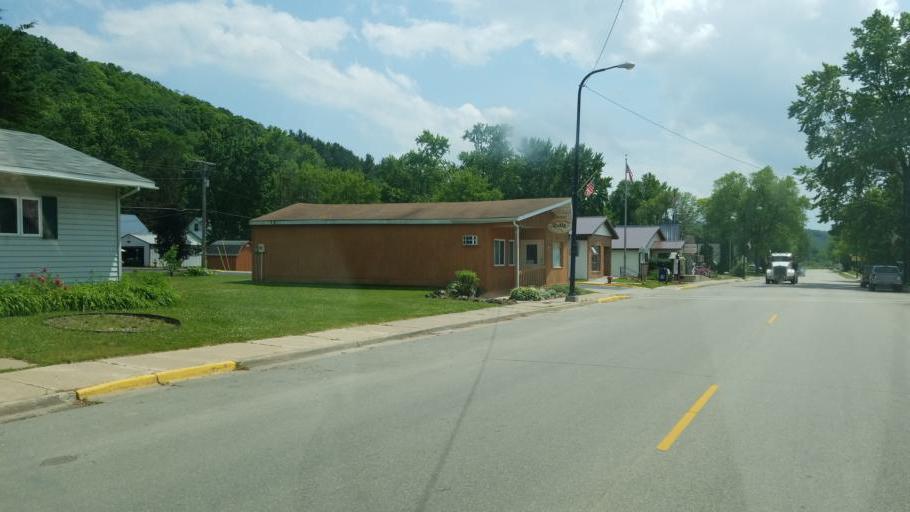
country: US
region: Wisconsin
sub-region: Vernon County
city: Viroqua
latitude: 43.4505
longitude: -90.7593
